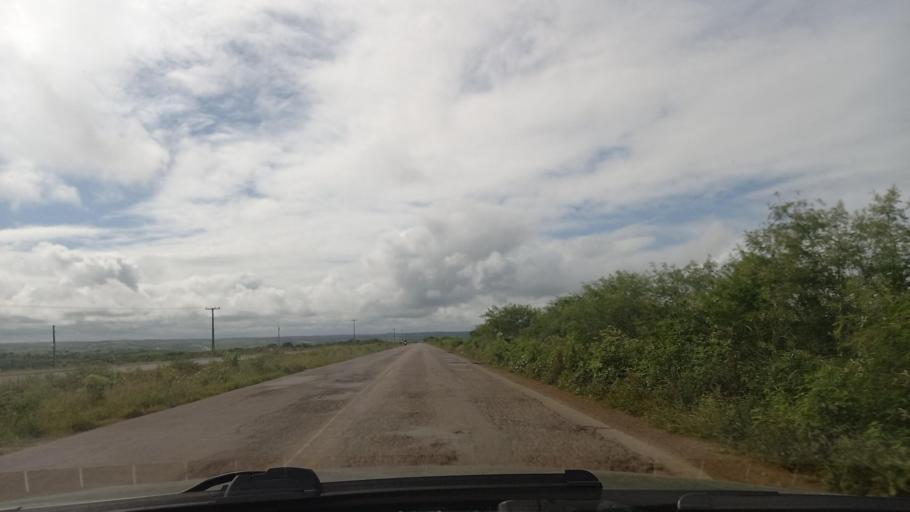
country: BR
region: Alagoas
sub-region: Batalha
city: Batalha
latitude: -9.6655
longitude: -37.1579
